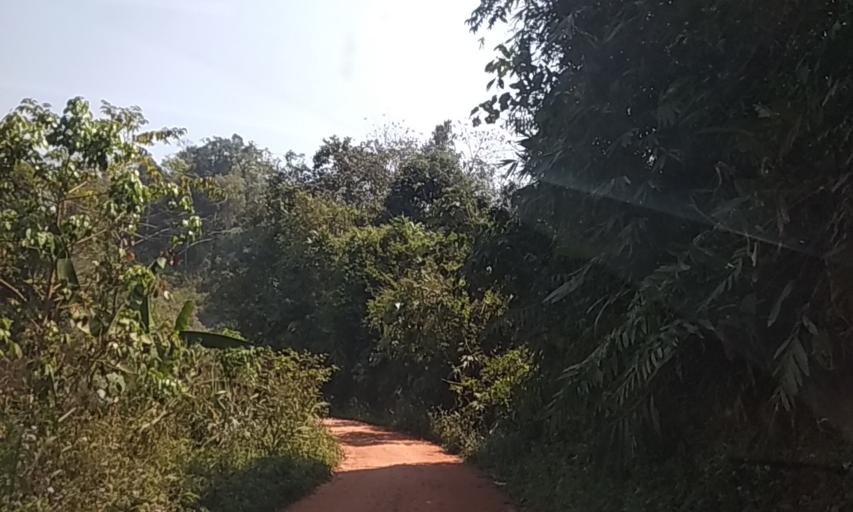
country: CN
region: Yunnan
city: Mengla
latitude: 21.5317
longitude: 101.8311
